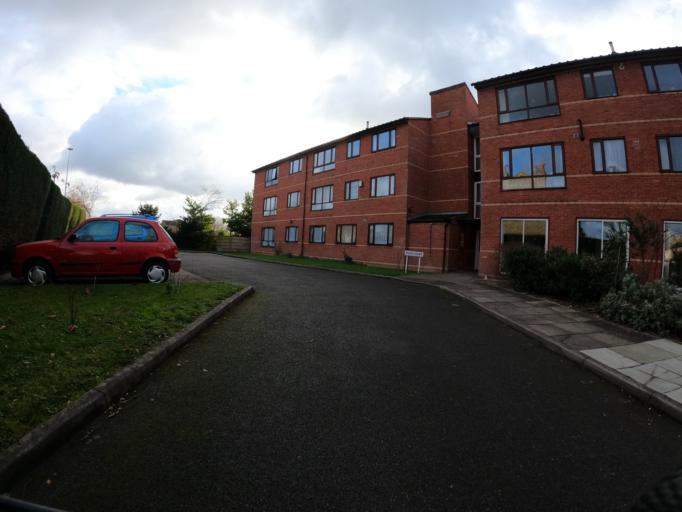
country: GB
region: England
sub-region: Greater London
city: Brentford
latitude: 51.4994
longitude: -0.3171
